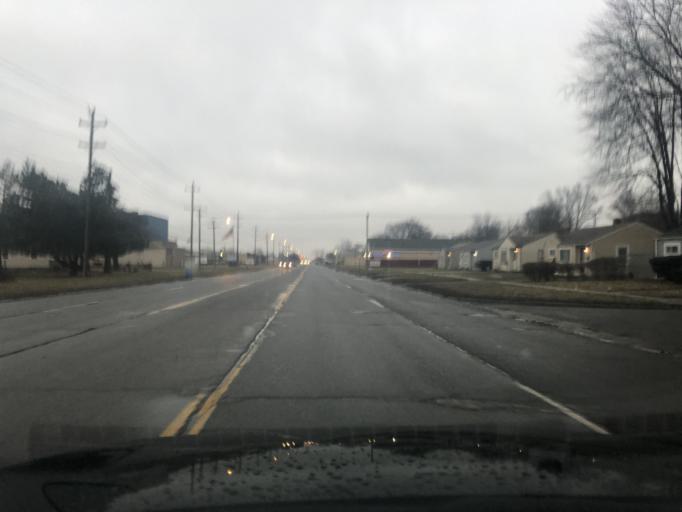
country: US
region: Michigan
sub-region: Wayne County
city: Inkster
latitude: 42.2683
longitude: -83.3057
